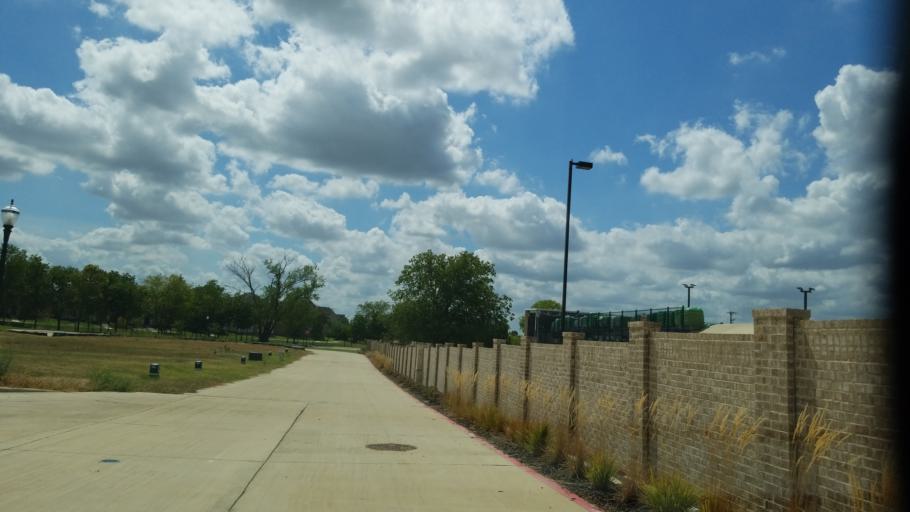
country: US
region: Texas
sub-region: Tarrant County
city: Euless
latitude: 32.8355
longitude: -97.0968
